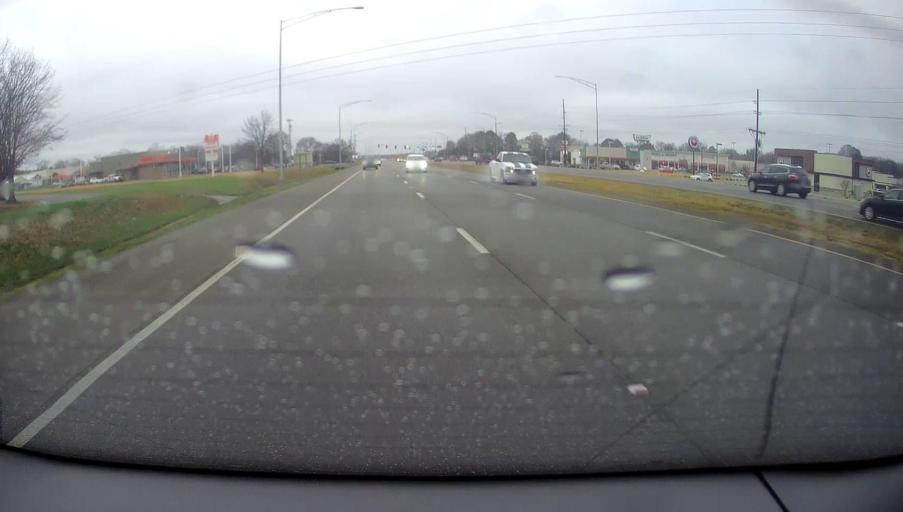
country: US
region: Alabama
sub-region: Morgan County
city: Decatur
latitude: 34.5657
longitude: -87.0108
